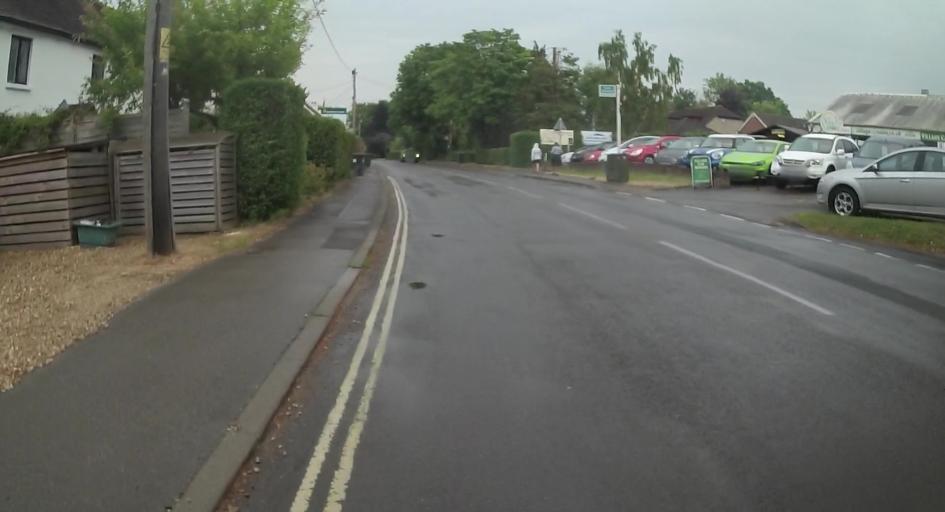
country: GB
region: England
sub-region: Hampshire
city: Fleet
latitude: 51.2663
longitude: -0.8636
